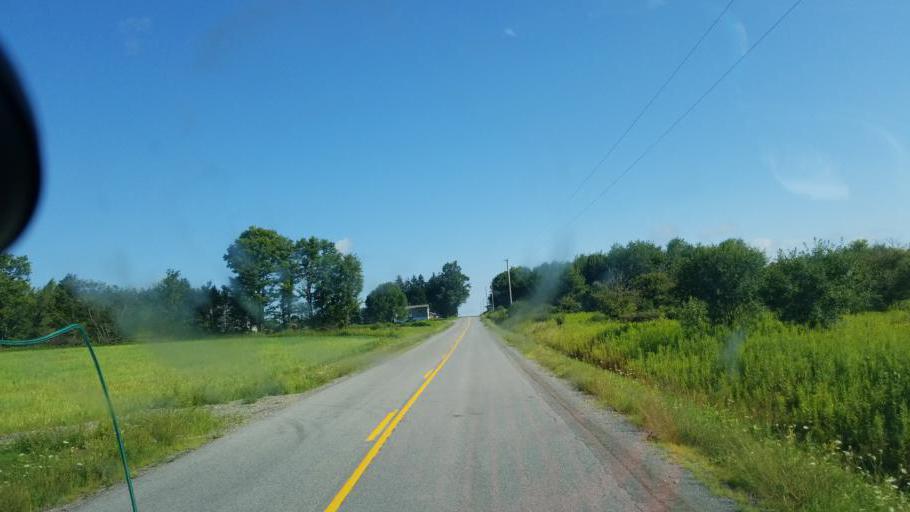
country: US
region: New York
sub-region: Allegany County
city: Andover
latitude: 42.1669
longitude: -77.7131
